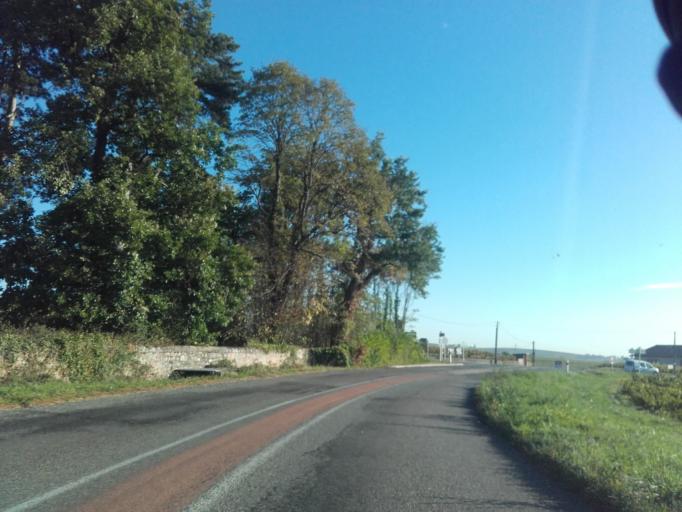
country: FR
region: Rhone-Alpes
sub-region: Departement du Rhone
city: Fleurie
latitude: 46.1765
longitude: 4.6906
